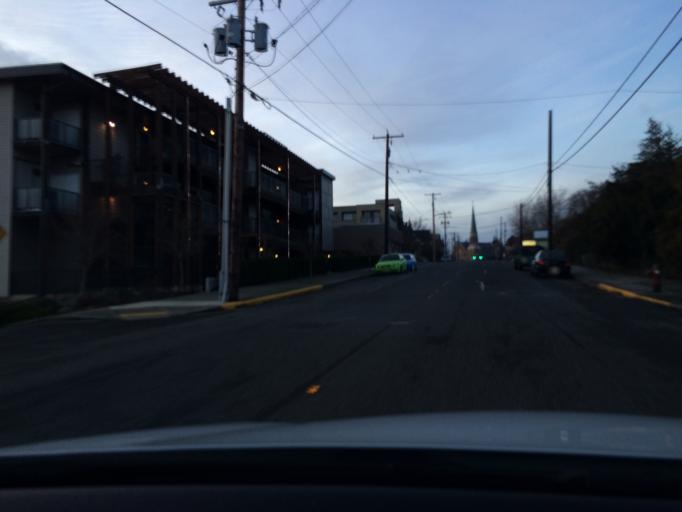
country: US
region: Washington
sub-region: Whatcom County
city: Bellingham
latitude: 48.7562
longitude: -122.4890
